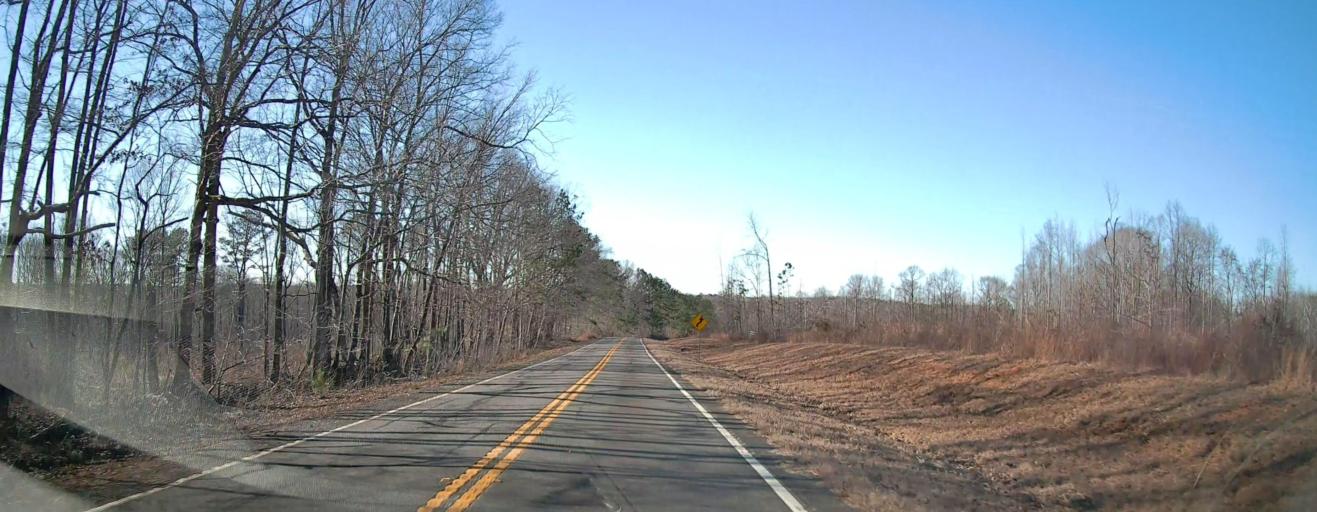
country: US
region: Georgia
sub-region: Talbot County
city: Talbotton
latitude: 32.6688
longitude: -84.4667
